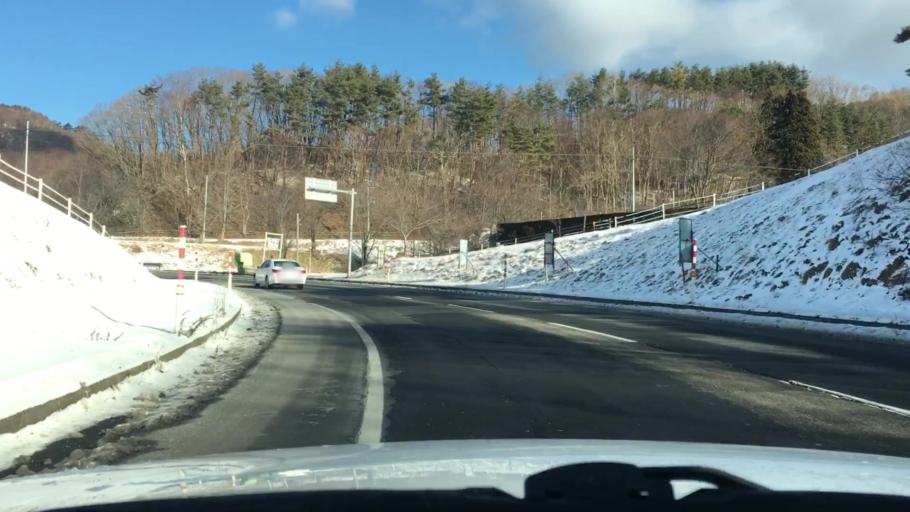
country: JP
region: Iwate
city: Morioka-shi
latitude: 39.6697
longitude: 141.3304
